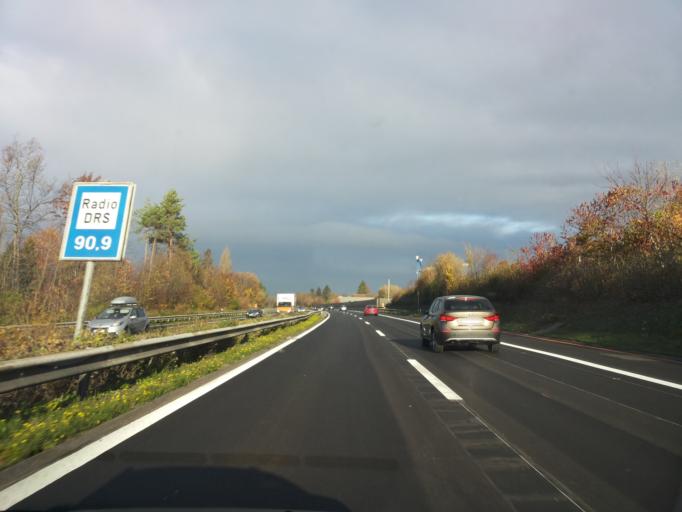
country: CH
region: Lucerne
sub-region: Sursee District
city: Schenkon
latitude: 47.1663
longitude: 8.1436
